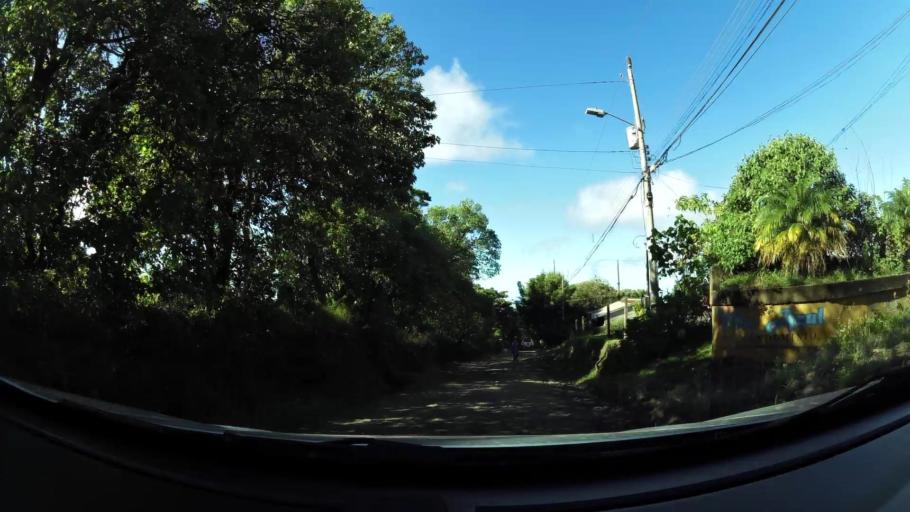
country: CR
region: Guanacaste
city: Juntas
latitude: 10.3151
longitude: -84.8301
